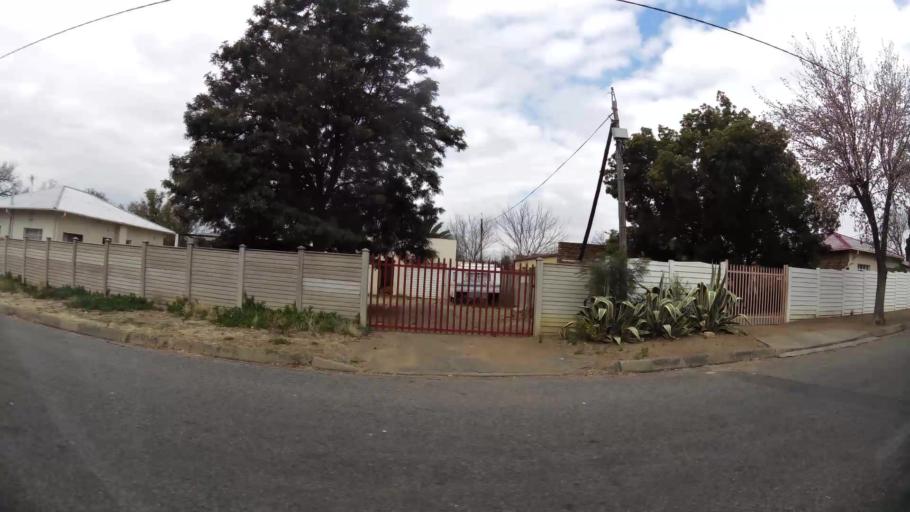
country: ZA
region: Orange Free State
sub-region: Fezile Dabi District Municipality
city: Kroonstad
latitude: -27.6447
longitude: 27.2353
